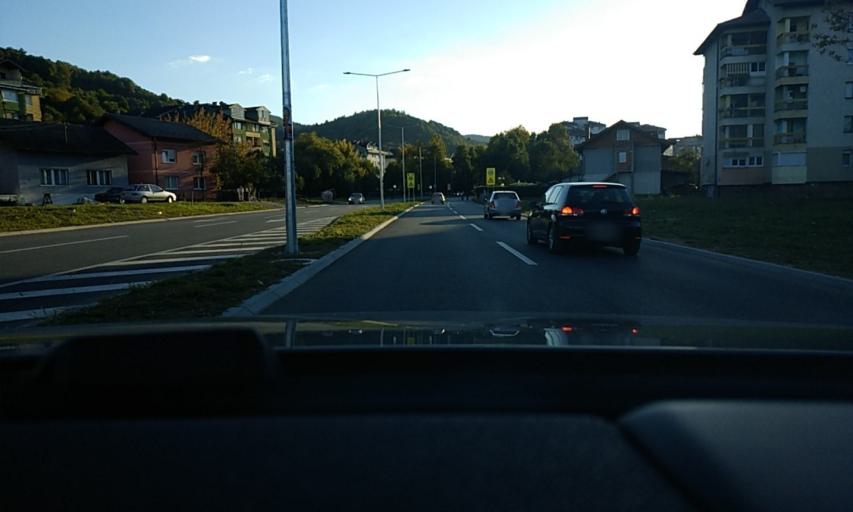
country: BA
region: Republika Srpska
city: Mejdan - Obilicevo
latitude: 44.7605
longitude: 17.1984
